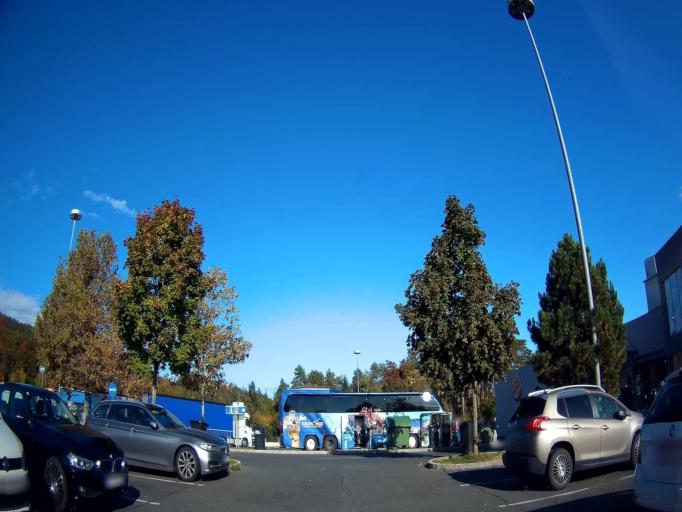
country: AT
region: Carinthia
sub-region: Politischer Bezirk Klagenfurt Land
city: Schiefling am See
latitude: 46.6288
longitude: 14.0942
